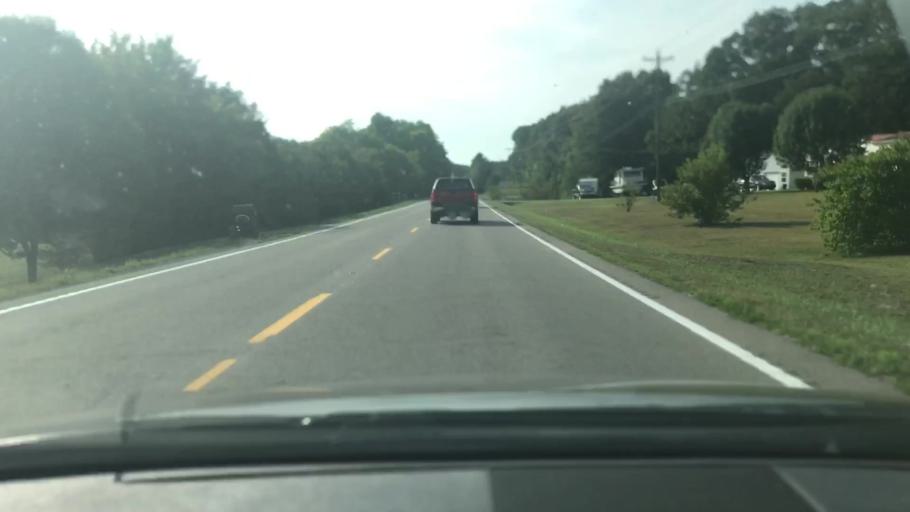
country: US
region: Tennessee
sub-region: Williamson County
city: Fairview
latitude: 36.0135
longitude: -87.1527
